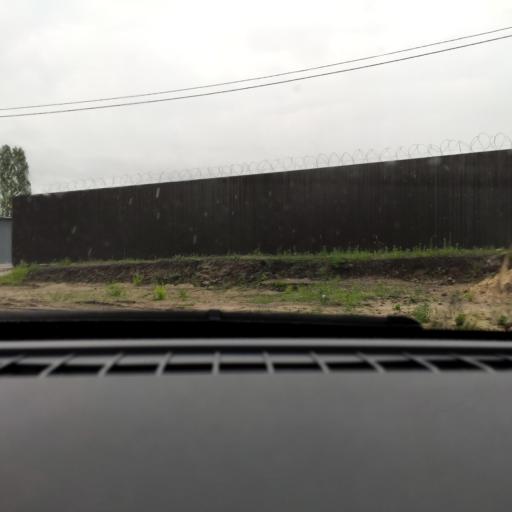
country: RU
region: Voronezj
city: Somovo
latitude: 51.7142
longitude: 39.2880
